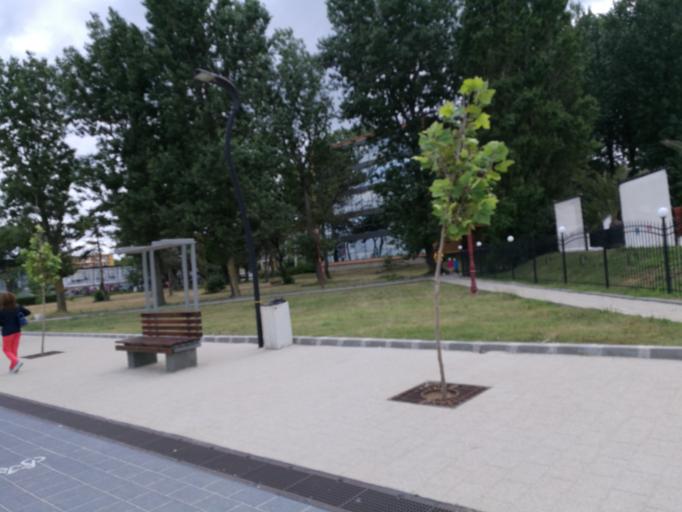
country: RO
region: Constanta
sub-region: Municipiul Constanta
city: Palazu Mare
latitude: 44.2533
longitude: 28.6217
